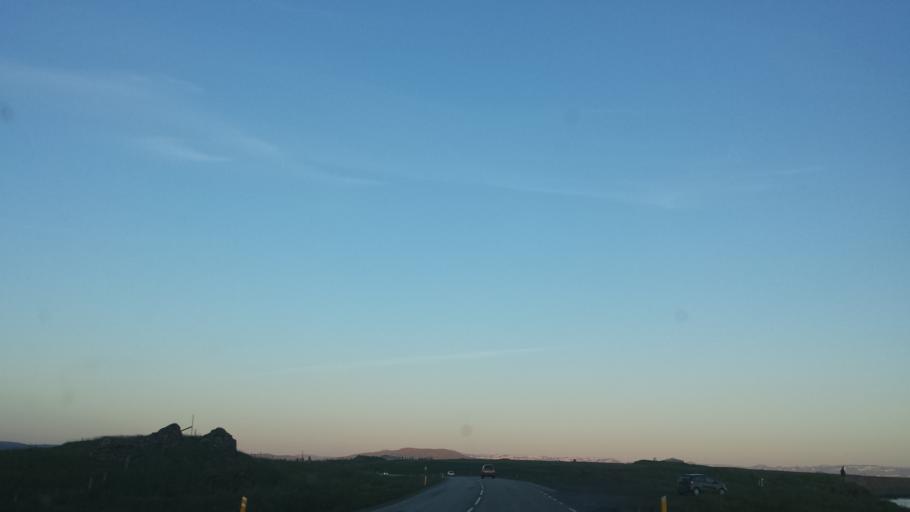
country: IS
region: Capital Region
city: Reykjavik
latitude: 64.2268
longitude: -21.8138
